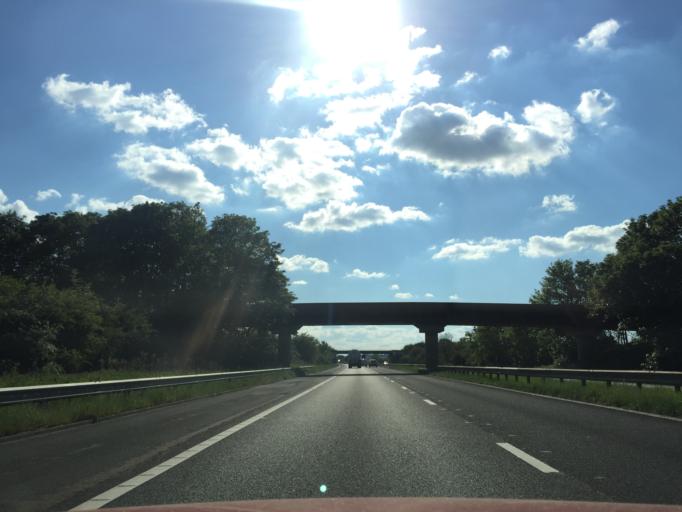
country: GB
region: England
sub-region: Warwickshire
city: Rugby
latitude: 52.3375
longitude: -1.2366
